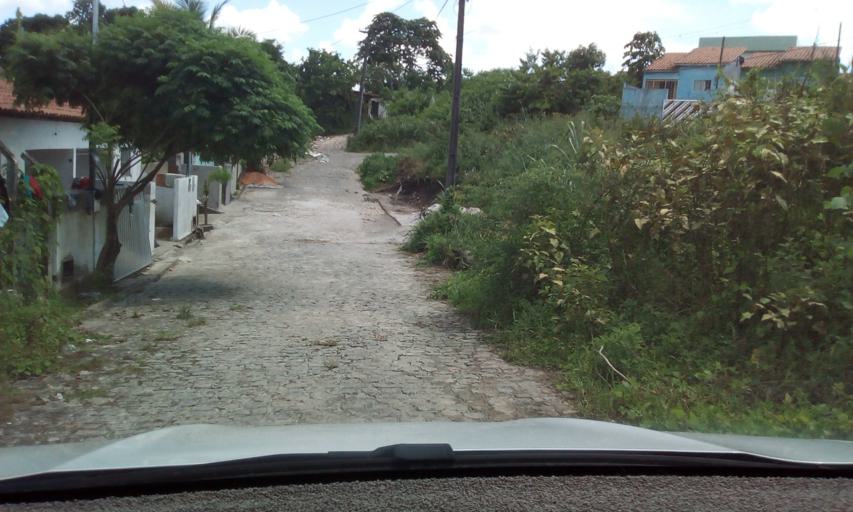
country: BR
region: Paraiba
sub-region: Bayeux
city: Bayeux
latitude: -7.1205
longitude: -34.9330
